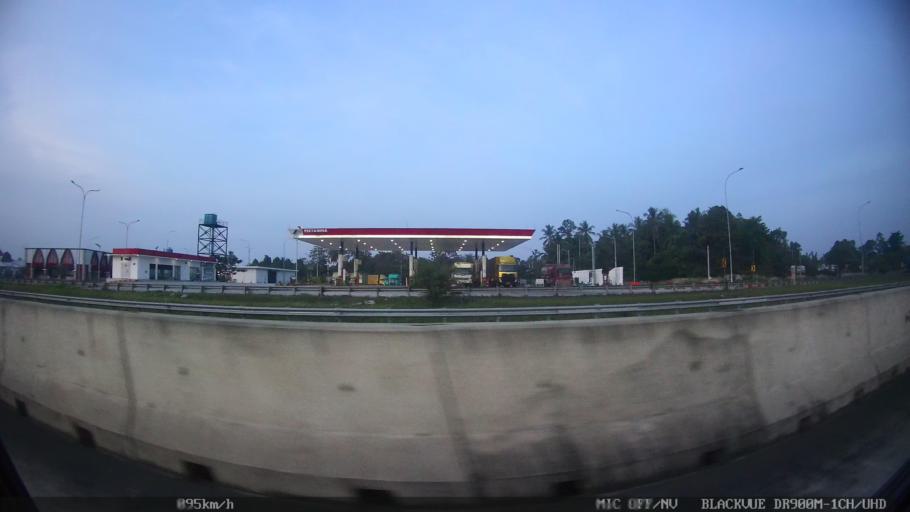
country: ID
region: Lampung
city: Pasuruan
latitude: -5.7271
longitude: 105.6692
